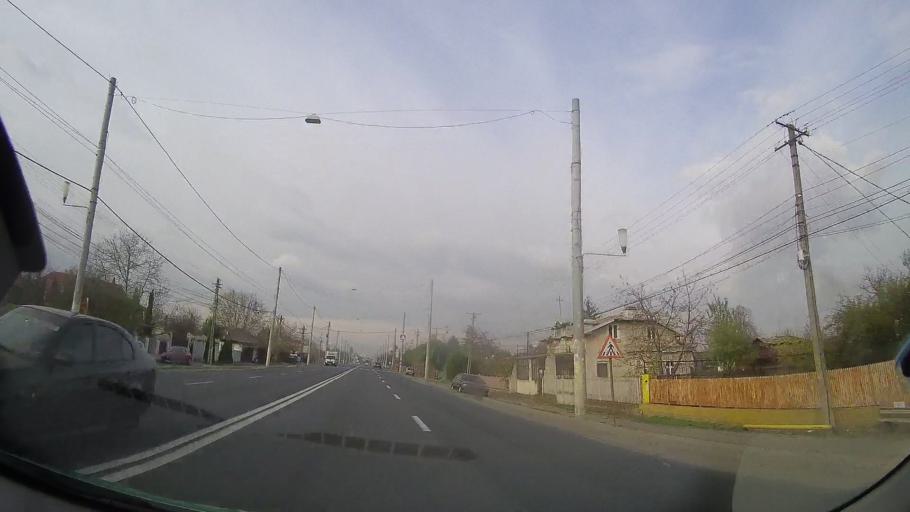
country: RO
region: Prahova
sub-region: Comuna Barcanesti
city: Tatarani
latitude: 44.8954
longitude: 26.0430
